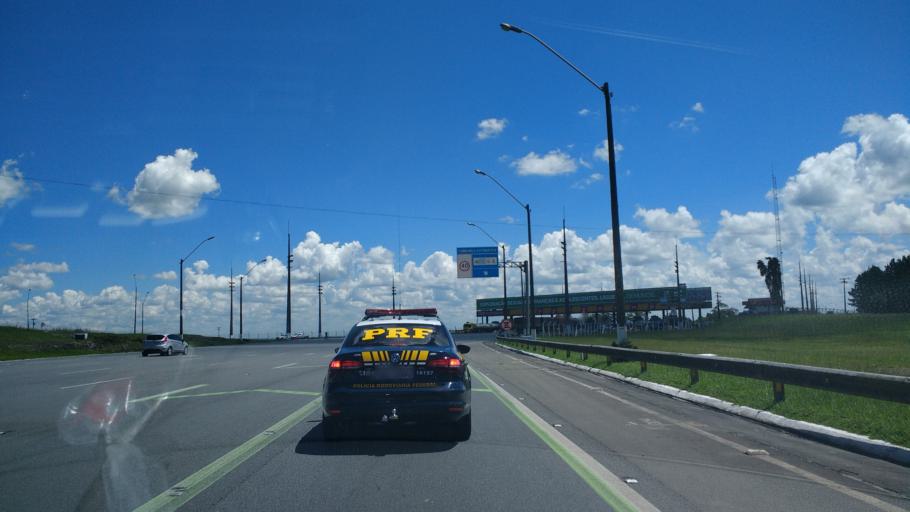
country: BR
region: Parana
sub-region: Campo Largo
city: Campo Largo
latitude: -25.4702
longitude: -49.6599
